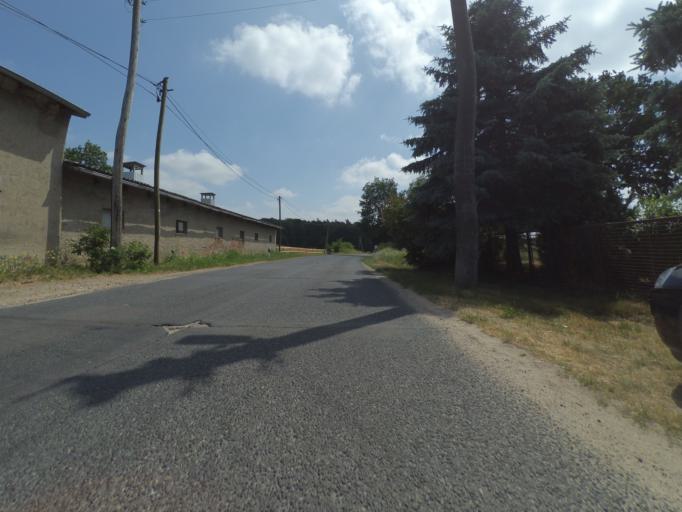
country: DE
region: Mecklenburg-Vorpommern
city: Plau am See
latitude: 53.4099
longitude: 12.3230
